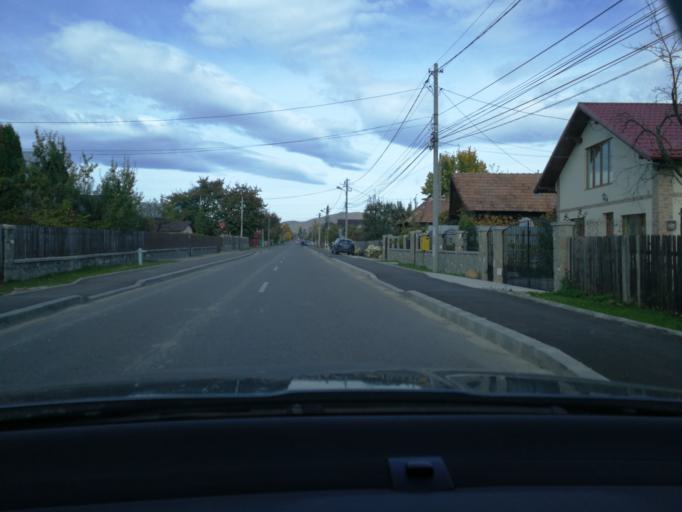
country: RO
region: Prahova
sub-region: Comuna Brebu
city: Brebu Megiesesc
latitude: 45.1635
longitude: 25.7746
